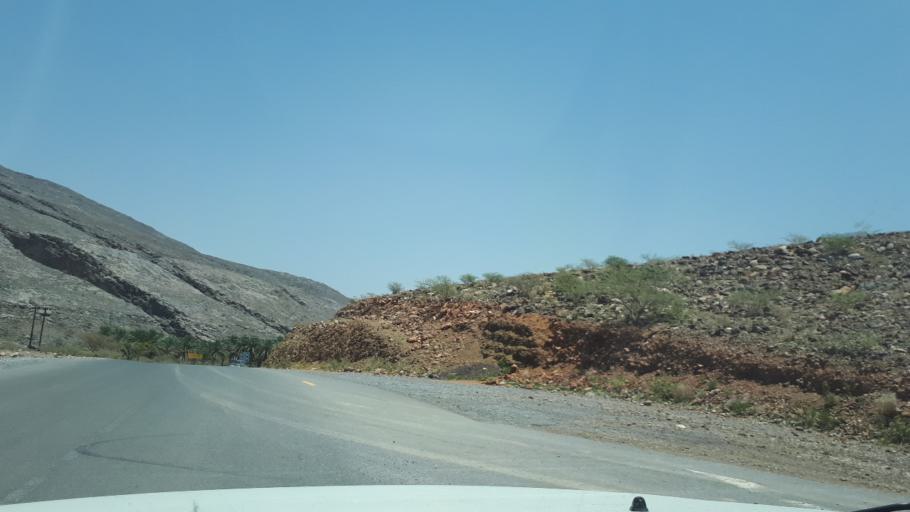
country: OM
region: Muhafazat ad Dakhiliyah
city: Bahla'
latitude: 23.1734
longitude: 57.1490
